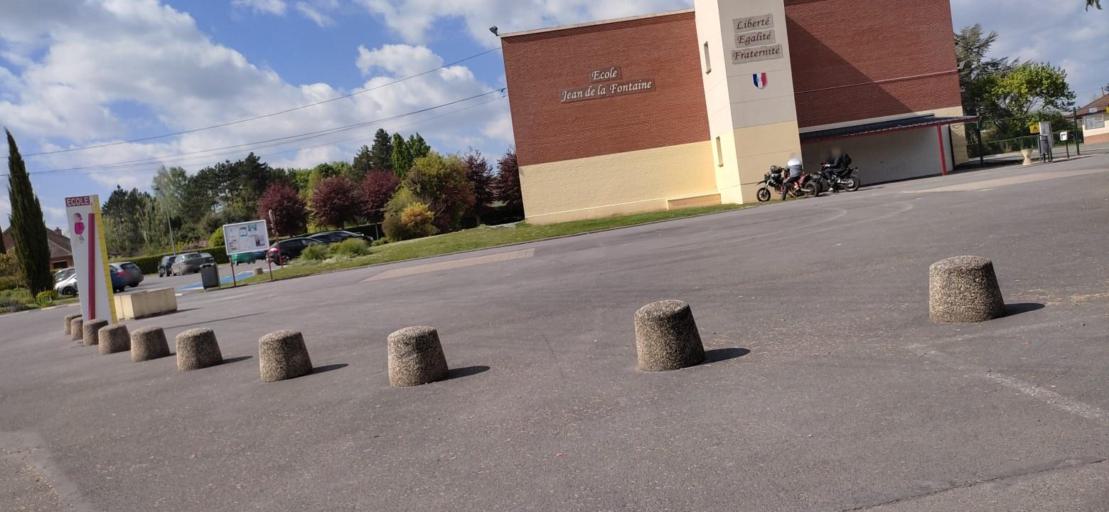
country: FR
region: Nord-Pas-de-Calais
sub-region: Departement du Pas-de-Calais
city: Biache-Saint-Vaast
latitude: 50.3124
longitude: 2.9397
